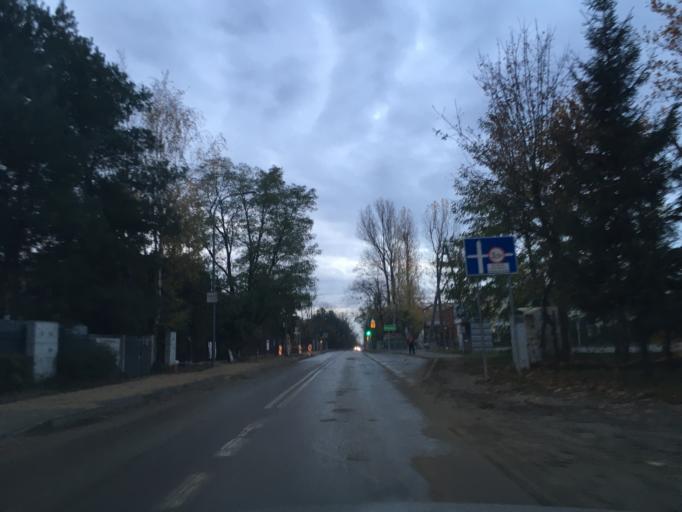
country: PL
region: Masovian Voivodeship
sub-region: Powiat piaseczynski
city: Piaseczno
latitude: 52.0567
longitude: 20.9828
